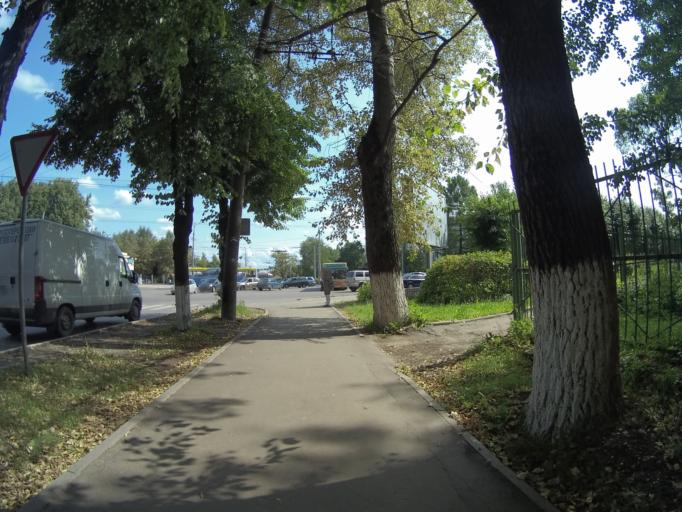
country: RU
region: Vladimir
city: Vladimir
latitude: 56.1414
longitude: 40.4057
